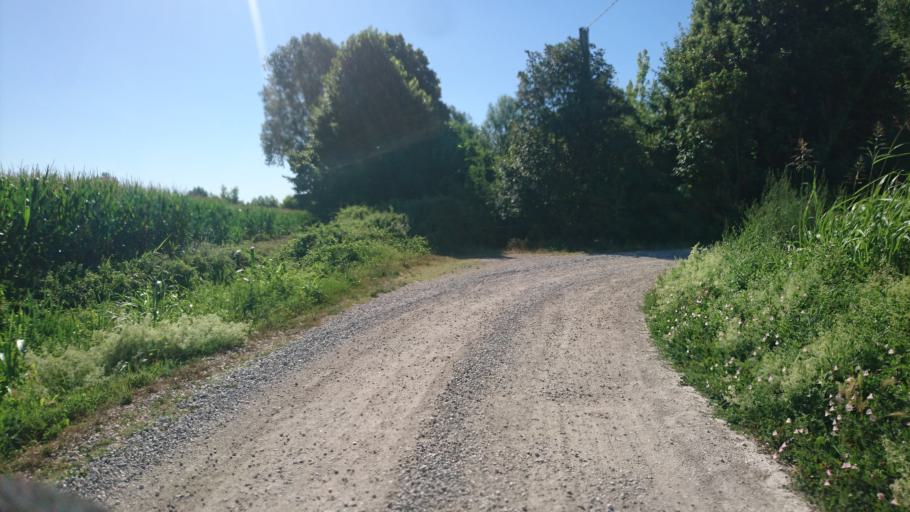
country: IT
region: Veneto
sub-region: Provincia di Padova
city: Legnaro
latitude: 45.3351
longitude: 11.9668
